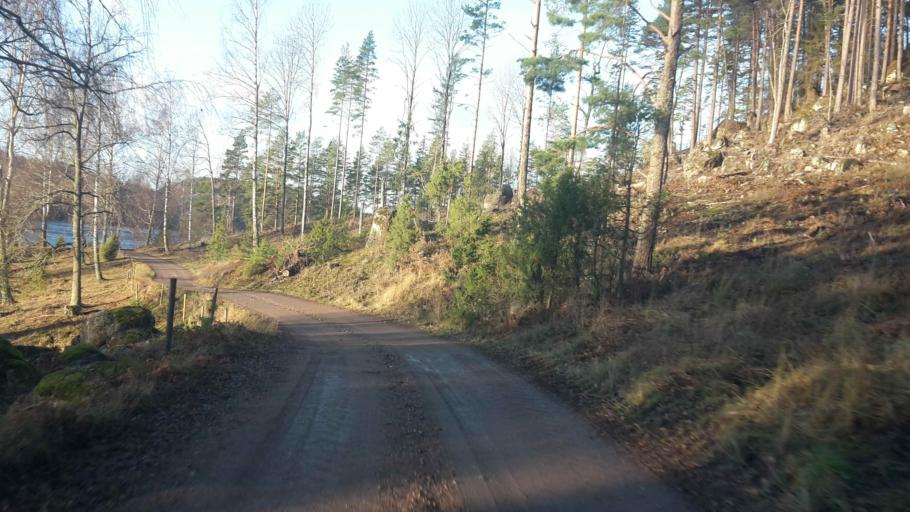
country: SE
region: OEstergoetland
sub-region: Atvidabergs Kommun
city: Atvidaberg
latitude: 58.2704
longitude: 16.1254
